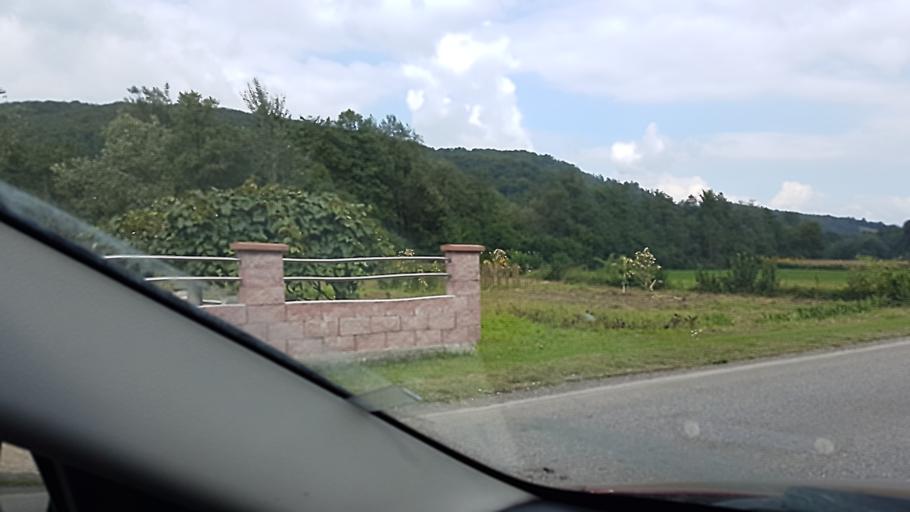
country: BA
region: Republika Srpska
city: Teslic
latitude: 44.6362
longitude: 17.8775
